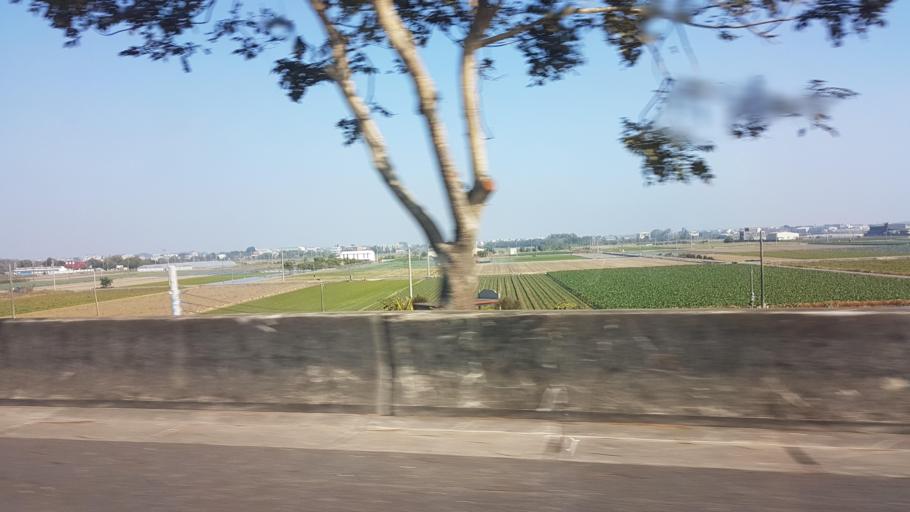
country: TW
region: Taiwan
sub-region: Chiayi
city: Taibao
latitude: 23.4205
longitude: 120.3760
